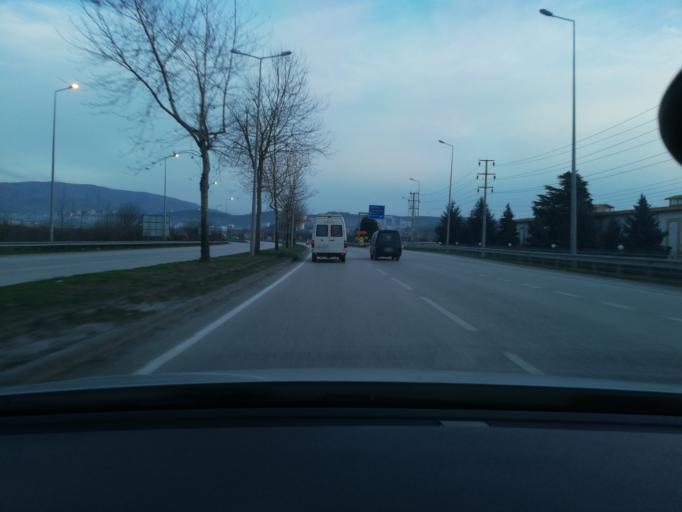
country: TR
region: Duzce
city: Konuralp
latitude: 40.8828
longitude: 31.1707
